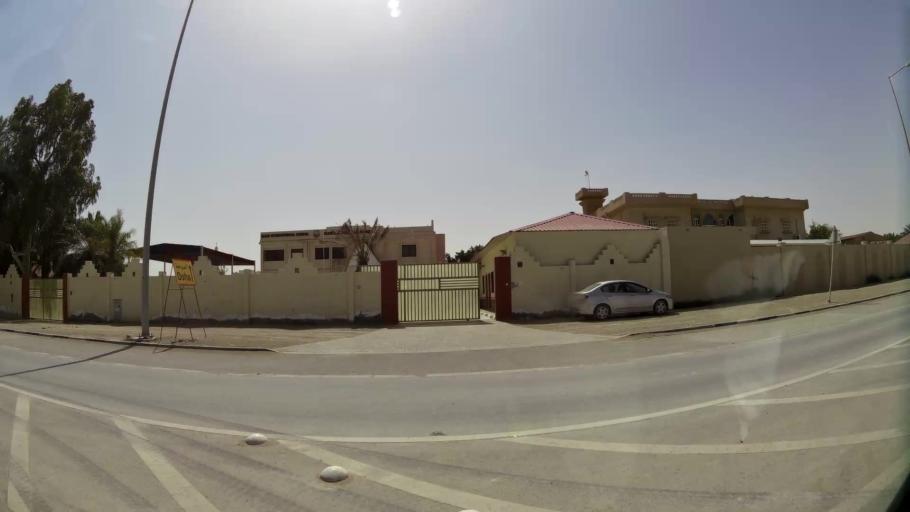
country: QA
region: Baladiyat Umm Salal
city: Umm Salal Muhammad
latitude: 25.3740
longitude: 51.4393
